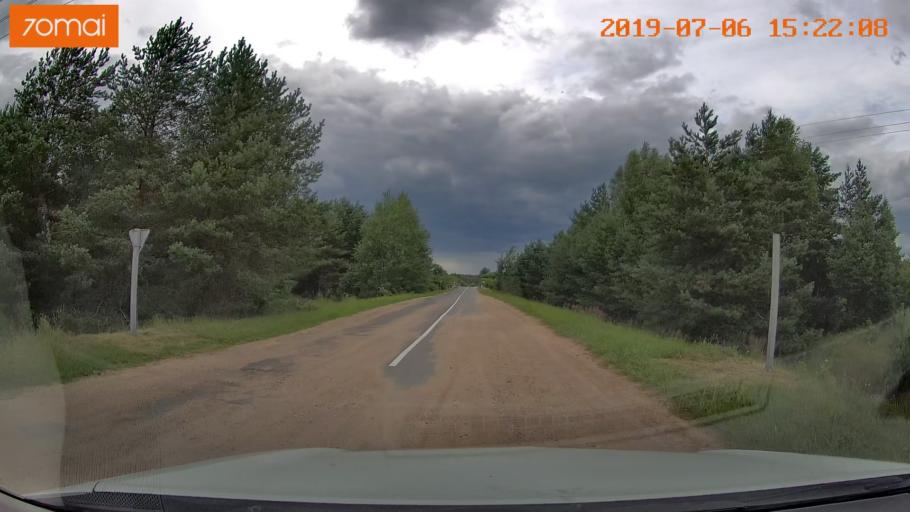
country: BY
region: Minsk
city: Valozhyn
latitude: 54.0116
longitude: 26.6065
